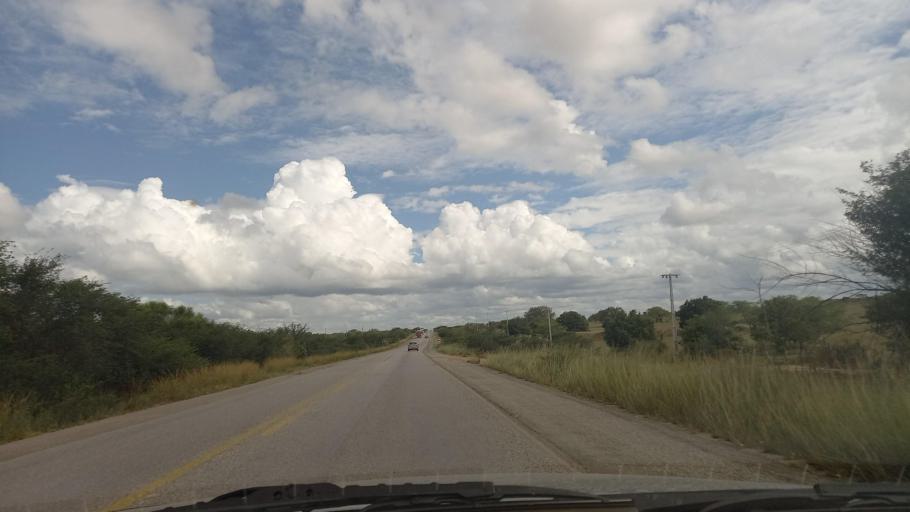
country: BR
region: Pernambuco
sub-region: Cachoeirinha
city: Cachoeirinha
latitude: -8.4310
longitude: -36.2000
